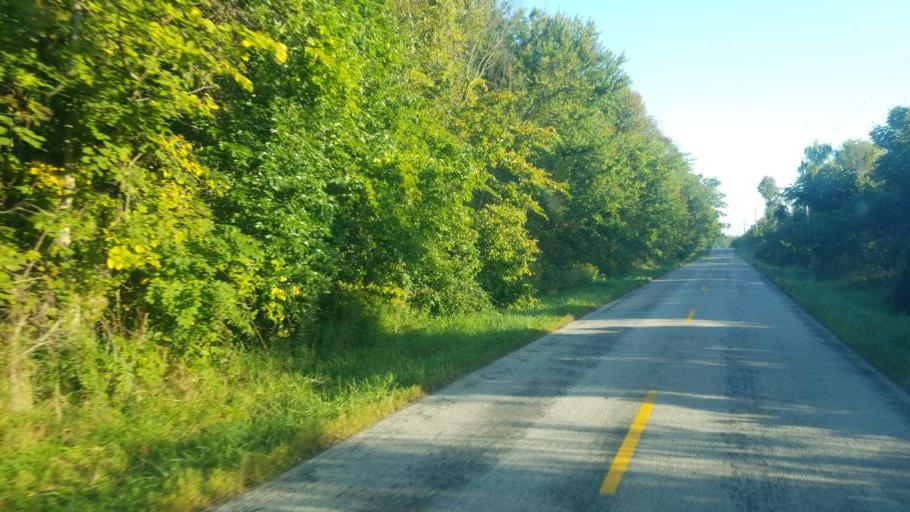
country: US
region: Ohio
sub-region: Lorain County
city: Wellington
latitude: 41.0630
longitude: -82.2583
